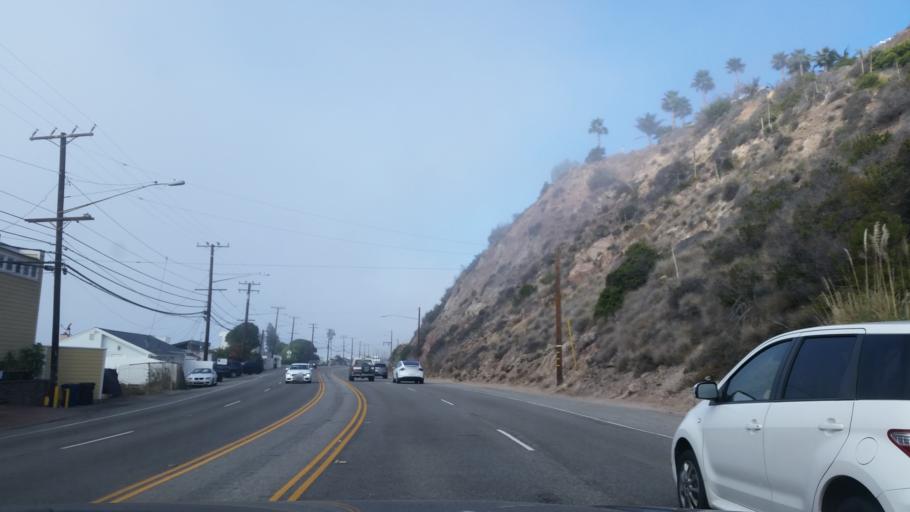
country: US
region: California
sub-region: Los Angeles County
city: Las Flores
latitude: 34.0372
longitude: -118.6119
